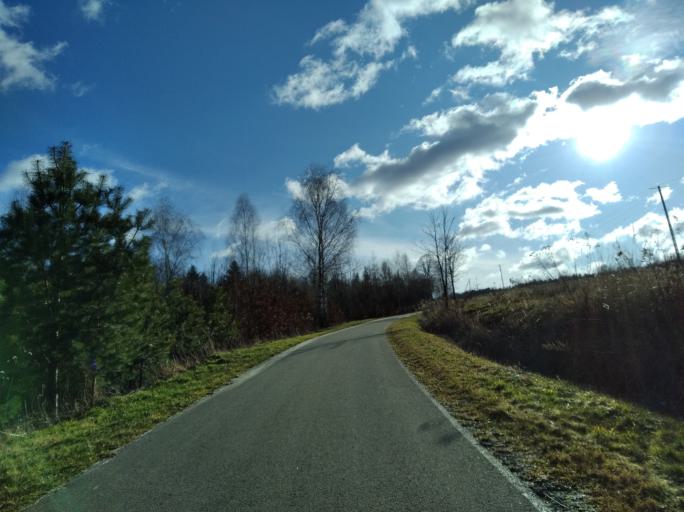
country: PL
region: Subcarpathian Voivodeship
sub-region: Powiat strzyzowski
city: Wisniowa
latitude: 49.9004
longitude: 21.6868
